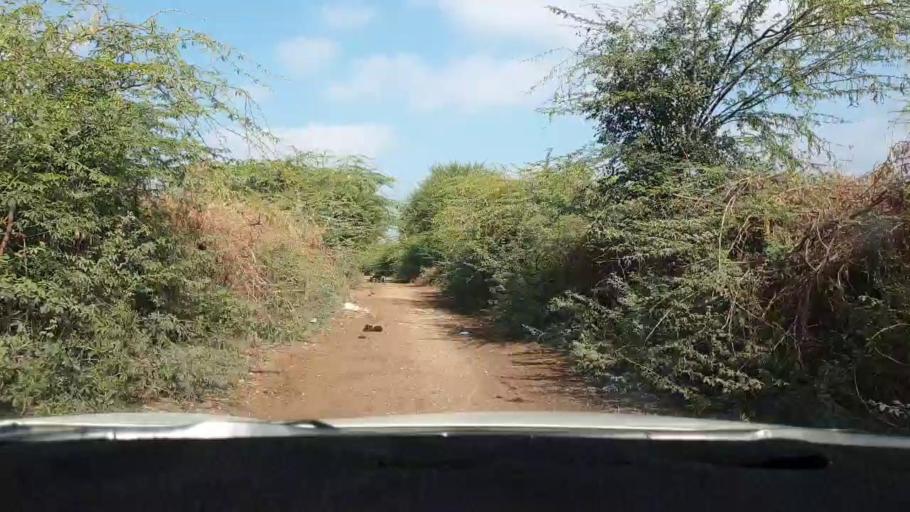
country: PK
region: Sindh
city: Berani
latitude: 25.7778
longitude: 68.9796
